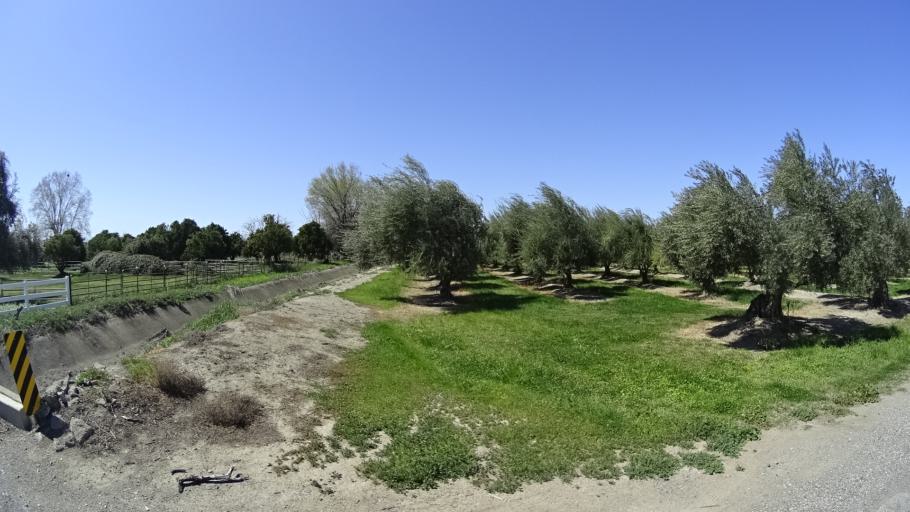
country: US
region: California
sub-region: Glenn County
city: Orland
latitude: 39.7661
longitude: -122.2388
